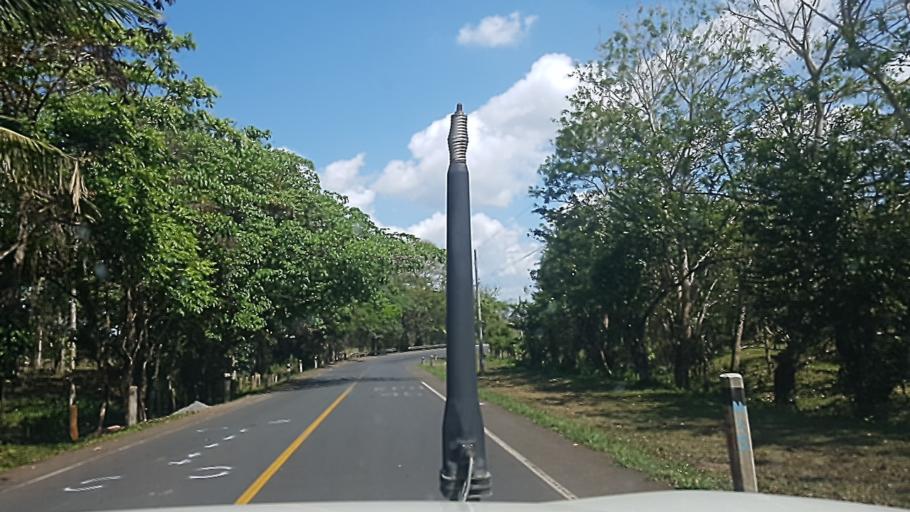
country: NI
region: Atlantico Sur
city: Muelle de los Bueyes
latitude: 11.9102
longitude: -84.6397
